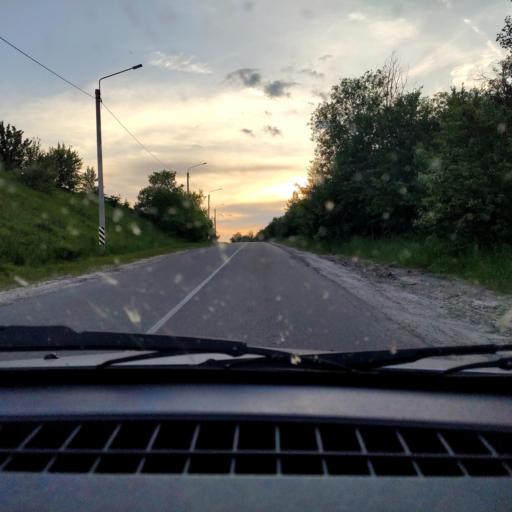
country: RU
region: Voronezj
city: Ramon'
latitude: 51.9511
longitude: 39.3686
